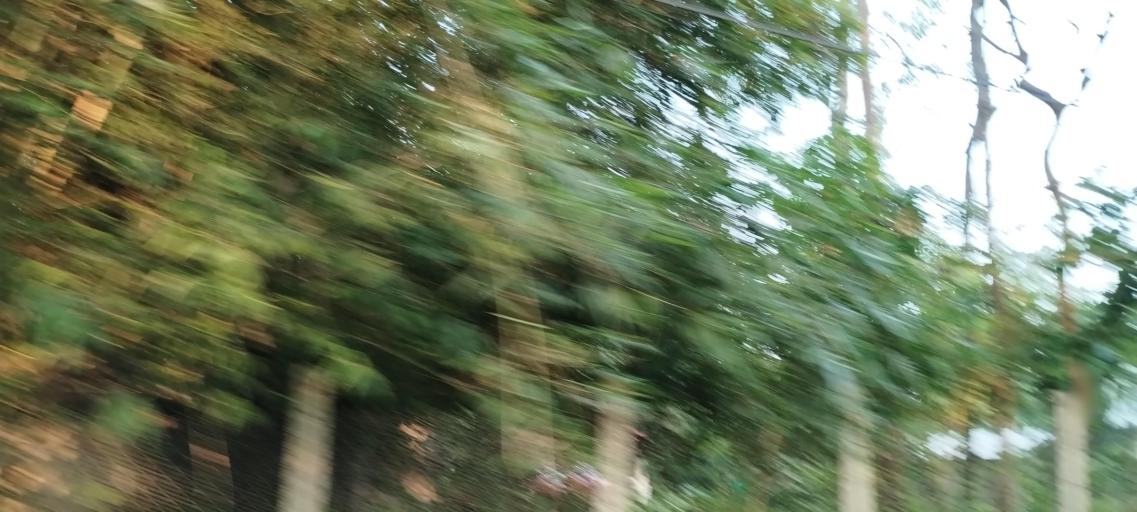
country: NP
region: Far Western
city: Tikapur
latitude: 28.4484
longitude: 81.2388
